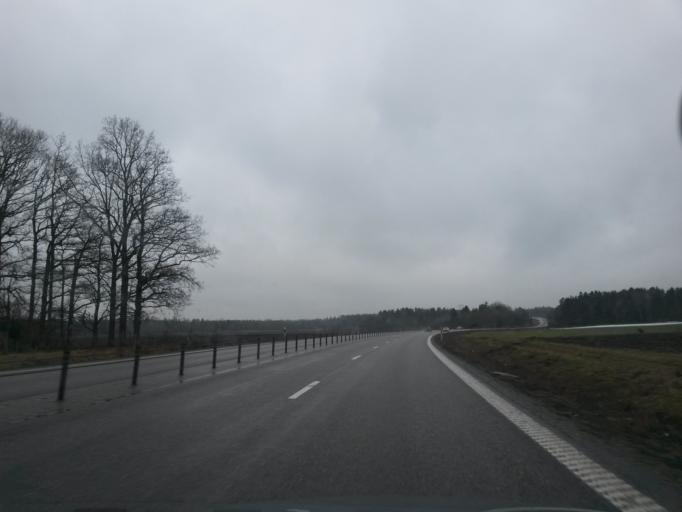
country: SE
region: Vaestra Goetaland
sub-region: Vanersborgs Kommun
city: Vanersborg
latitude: 58.3482
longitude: 12.3131
